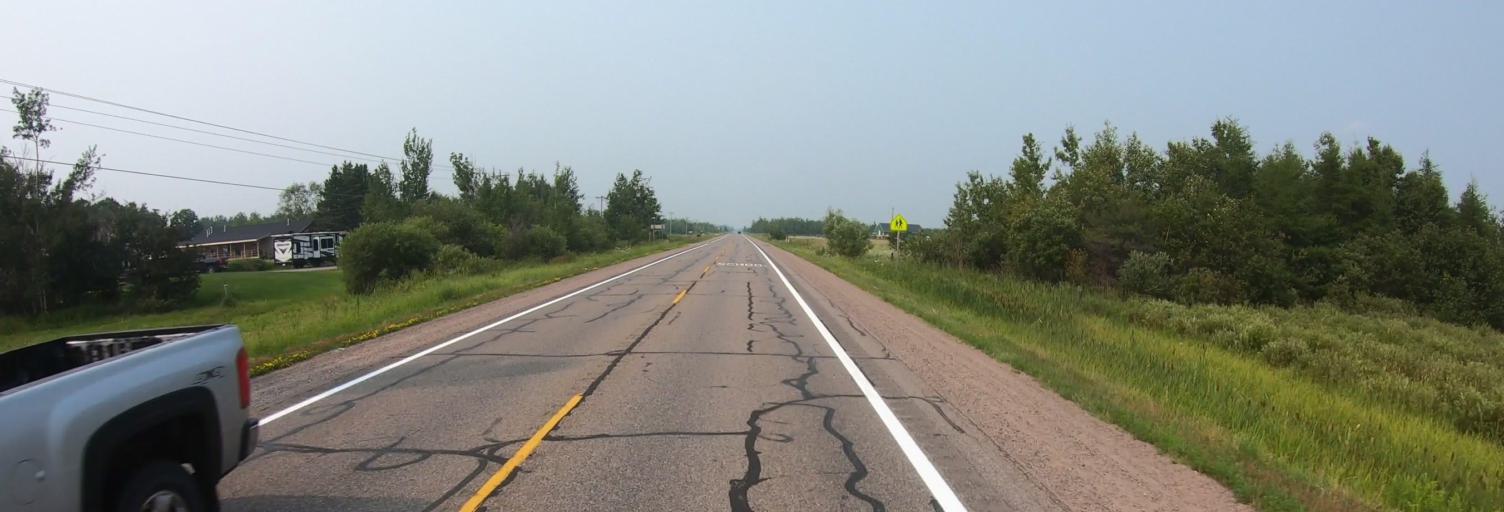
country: US
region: Michigan
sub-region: Chippewa County
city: Sault Ste. Marie
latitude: 46.4201
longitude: -84.3534
